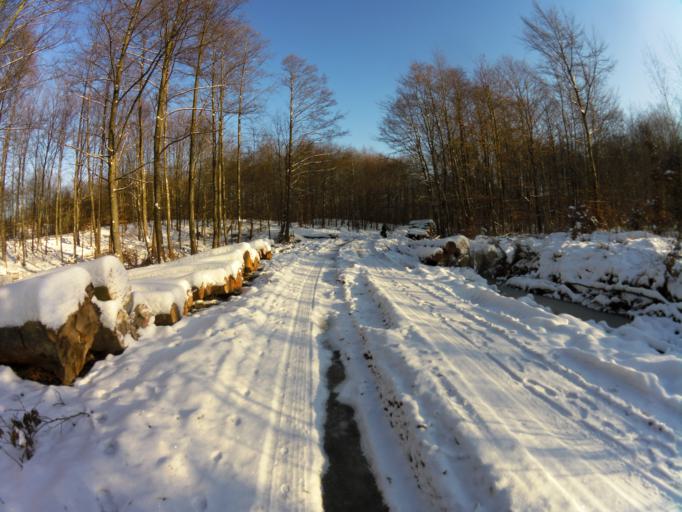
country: PL
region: West Pomeranian Voivodeship
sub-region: Powiat stargardzki
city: Insko
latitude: 53.3842
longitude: 15.5370
